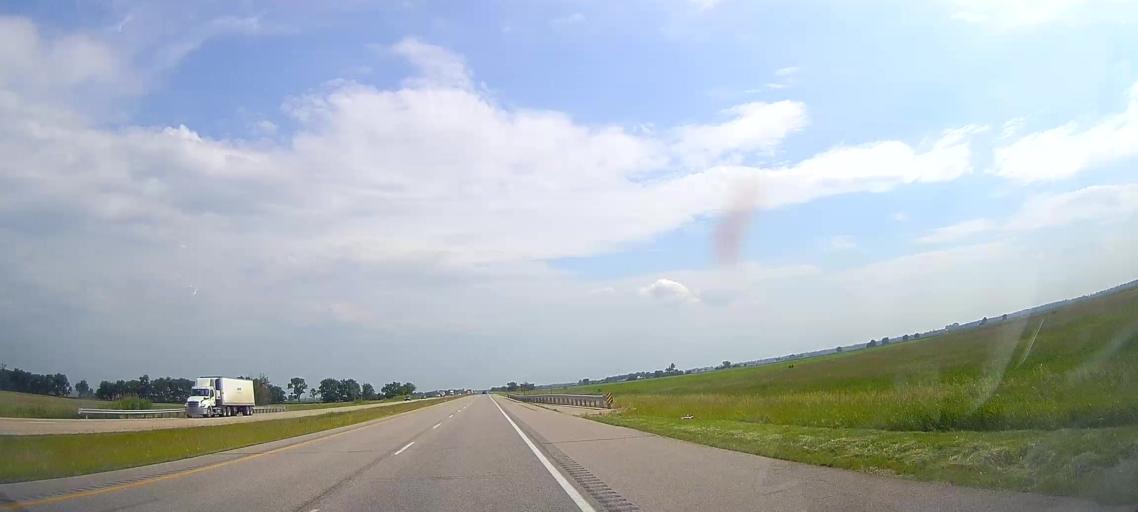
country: US
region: Iowa
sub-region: Monona County
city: Onawa
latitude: 41.9050
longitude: -96.1044
